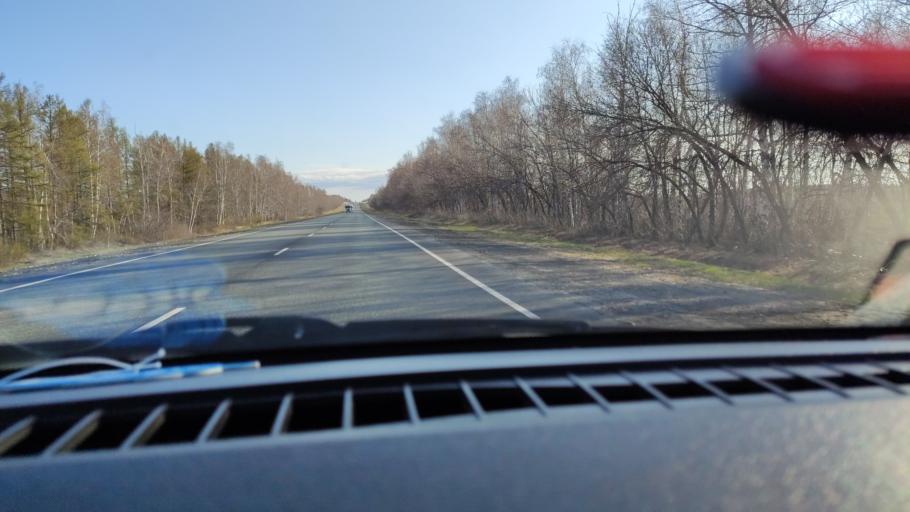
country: RU
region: Saratov
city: Khvalynsk
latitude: 52.5780
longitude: 48.1125
